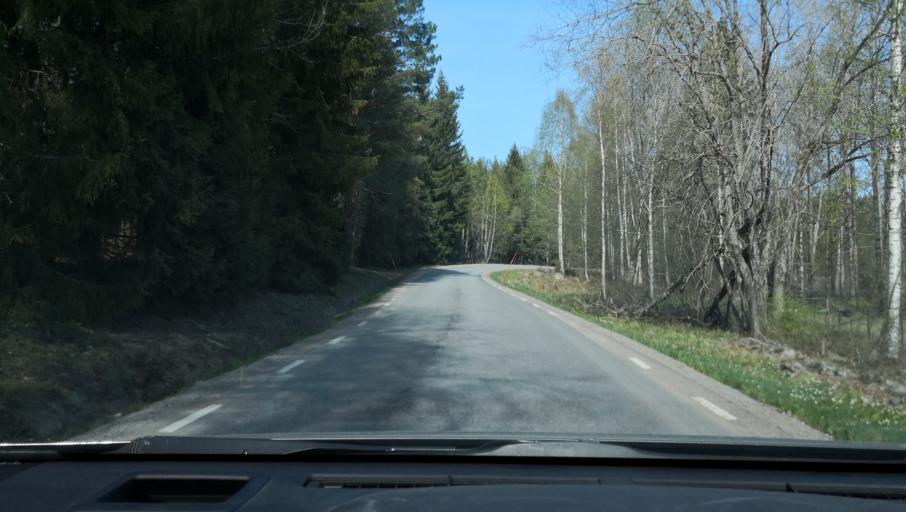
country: SE
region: Vaestmanland
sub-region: Sala Kommun
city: Sala
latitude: 59.9965
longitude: 16.6532
